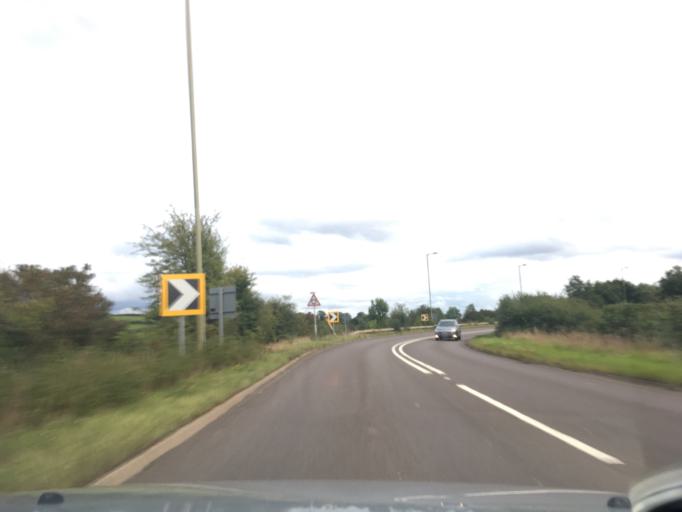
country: GB
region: England
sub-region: Oxfordshire
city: Banbury
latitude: 52.0753
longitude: -1.3112
